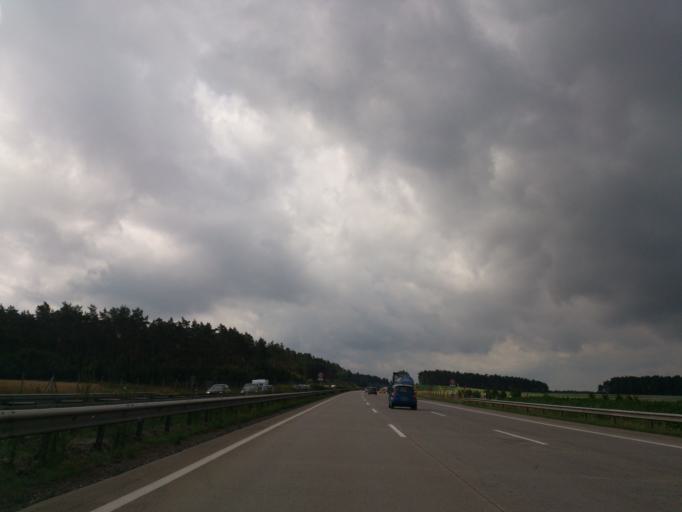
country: DE
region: Lower Saxony
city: Egestorf
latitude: 53.1788
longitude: 10.0806
